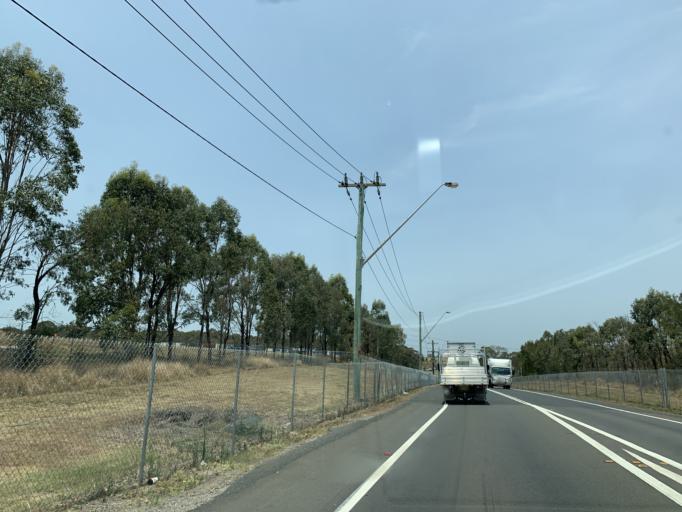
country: AU
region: New South Wales
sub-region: Fairfield
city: Horsley Park
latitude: -33.8111
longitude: 150.8663
